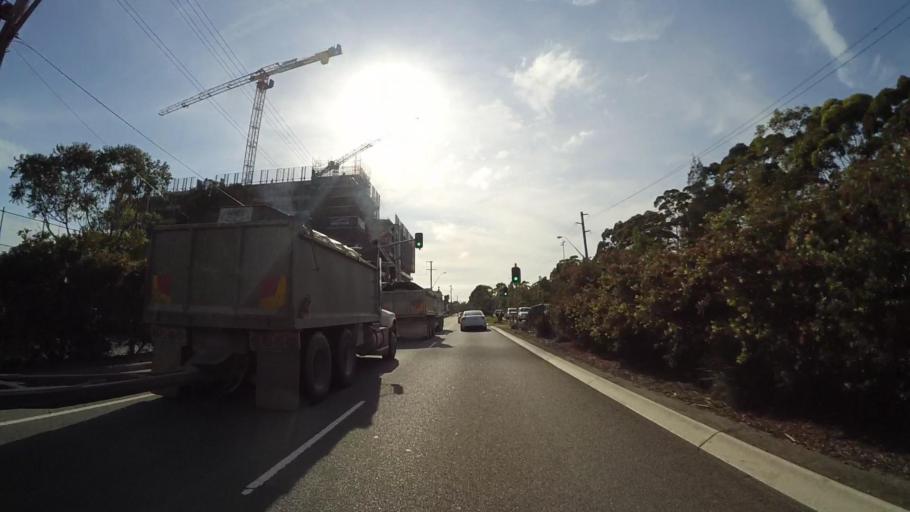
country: AU
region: New South Wales
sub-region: Sutherland Shire
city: Caringbah
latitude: -34.0390
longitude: 151.1370
